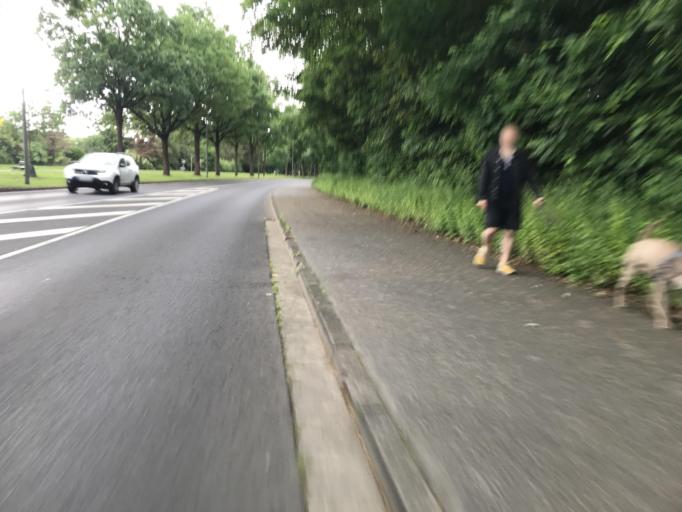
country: DE
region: Hesse
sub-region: Regierungsbezirk Kassel
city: Fuldabruck
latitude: 51.2963
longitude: 9.4418
